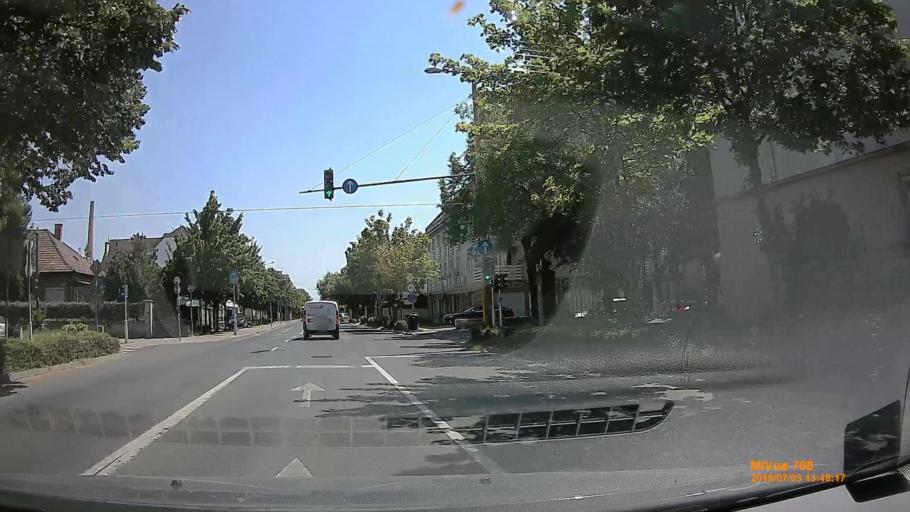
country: HU
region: Gyor-Moson-Sopron
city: Gyor
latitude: 47.6825
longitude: 17.6429
